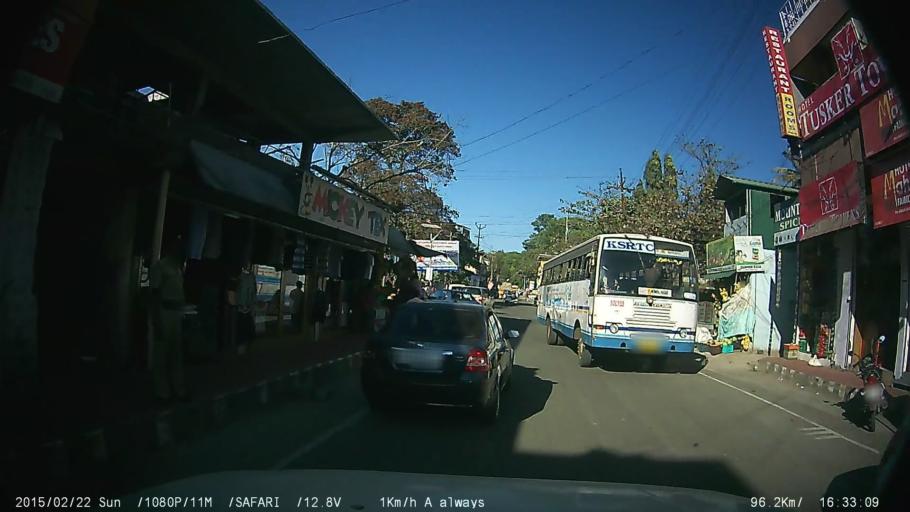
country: IN
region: Tamil Nadu
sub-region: Theni
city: Gudalur
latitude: 9.6084
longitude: 77.1689
